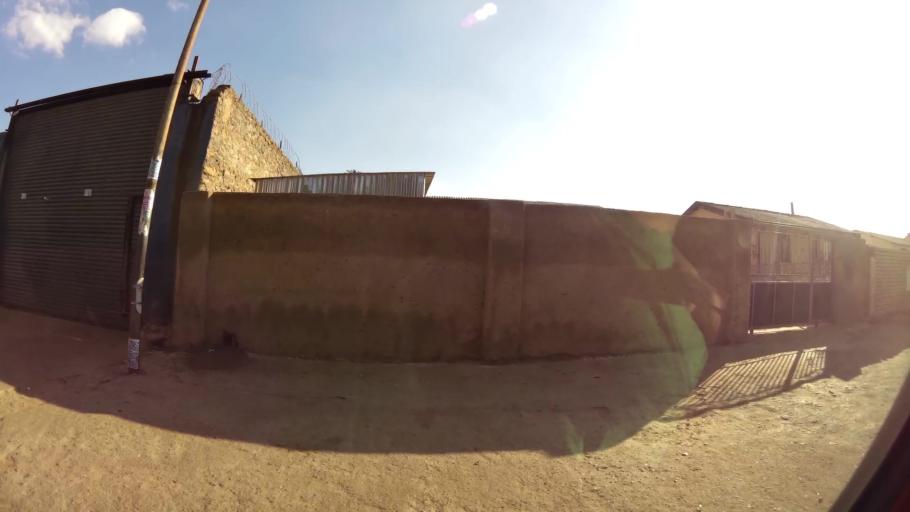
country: ZA
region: Gauteng
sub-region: City of Johannesburg Metropolitan Municipality
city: Soweto
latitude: -26.2198
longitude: 27.8724
